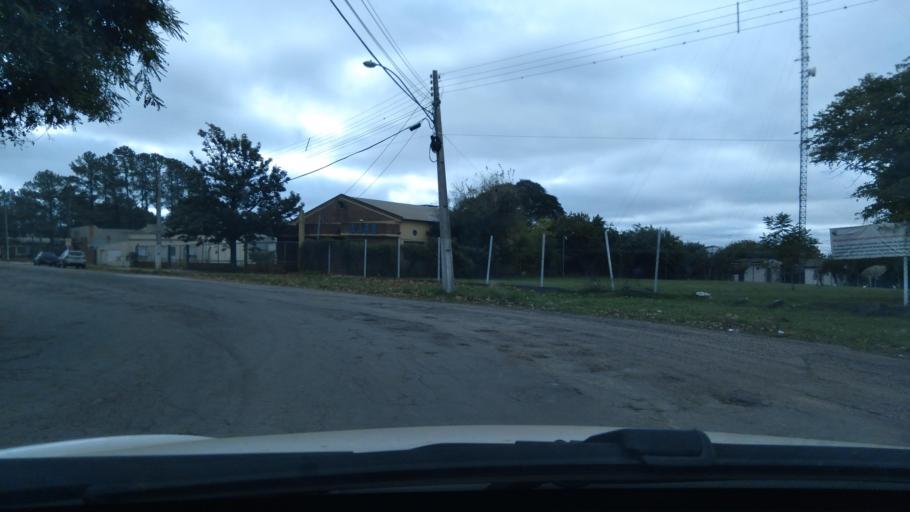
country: BR
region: Rio Grande do Sul
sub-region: Dom Pedrito
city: Dom Pedrito
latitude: -30.9679
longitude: -54.6725
